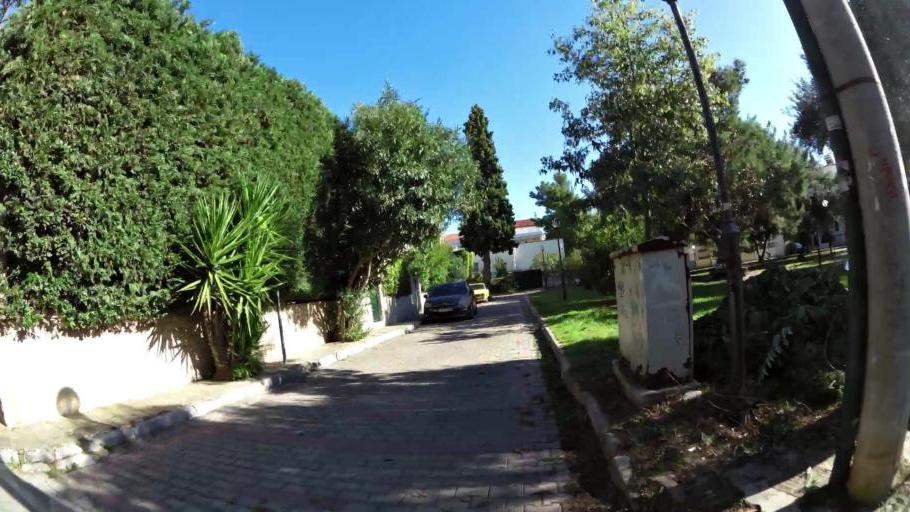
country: GR
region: Attica
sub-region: Nomarchia Athinas
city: Vrilissia
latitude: 38.0370
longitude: 23.8425
